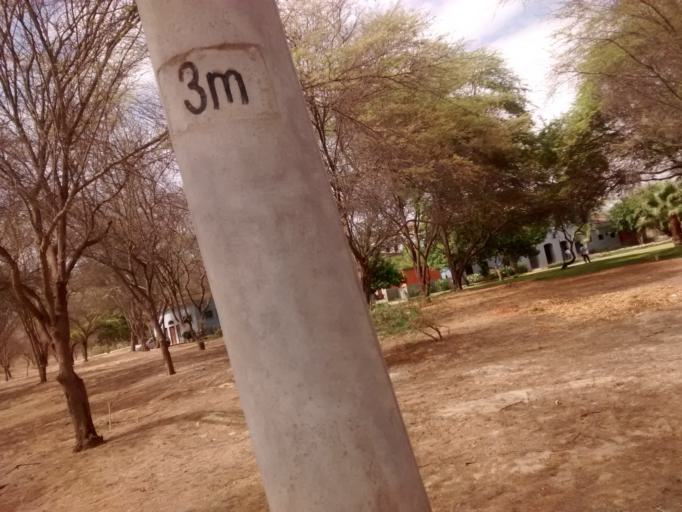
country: PE
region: Piura
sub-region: Provincia de Piura
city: Piura
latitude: -5.1786
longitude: -80.6358
